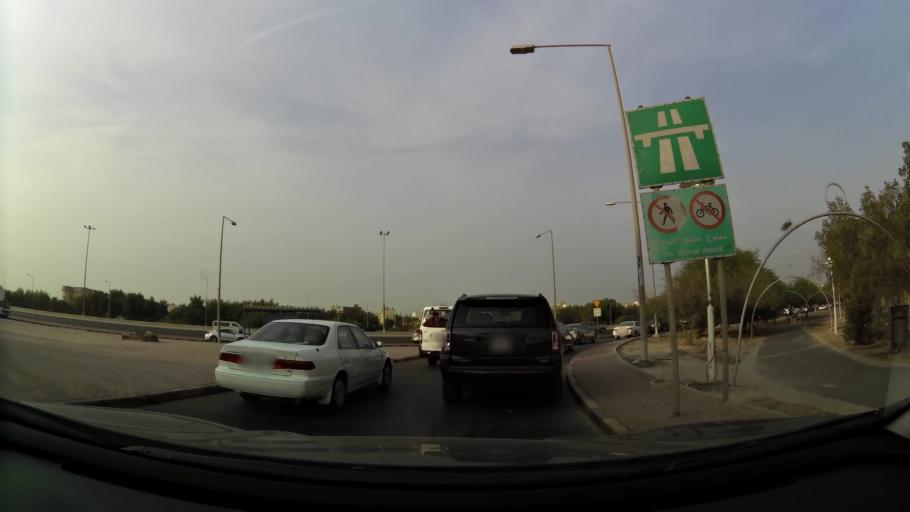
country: KW
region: Mubarak al Kabir
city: Sabah as Salim
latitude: 29.2660
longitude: 48.0762
